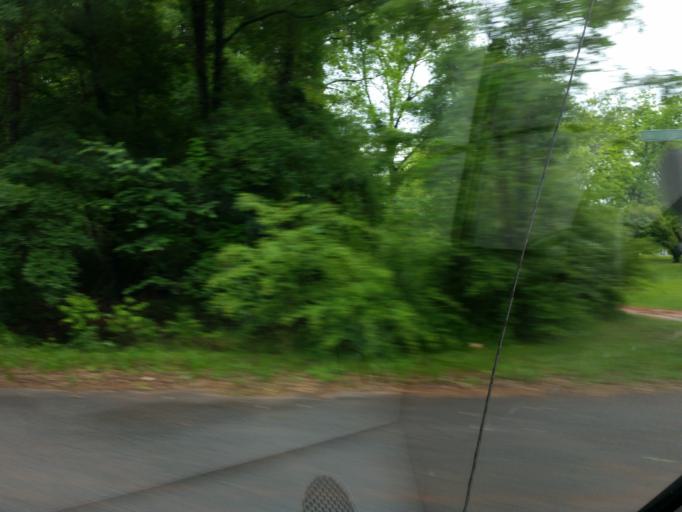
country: US
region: Georgia
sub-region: Peach County
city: Byron
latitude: 32.6551
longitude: -83.8047
